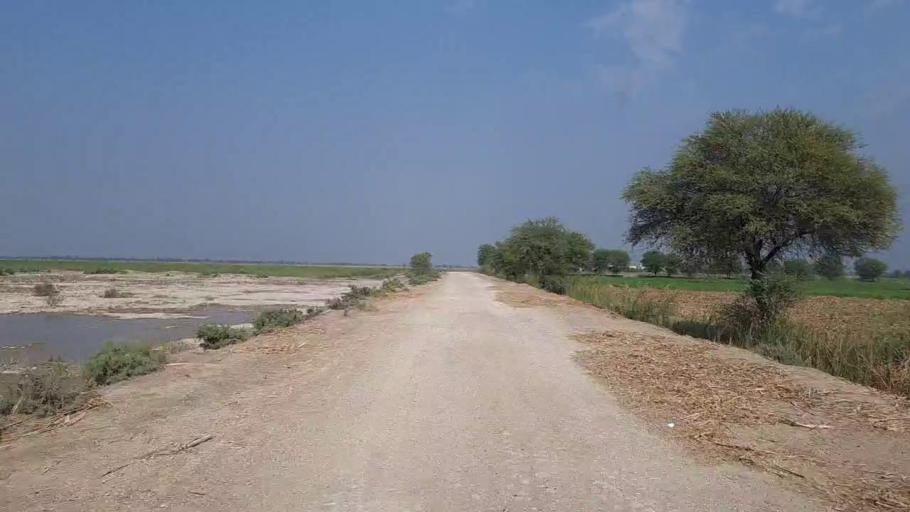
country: PK
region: Sindh
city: Mirwah Gorchani
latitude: 25.3754
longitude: 69.0400
